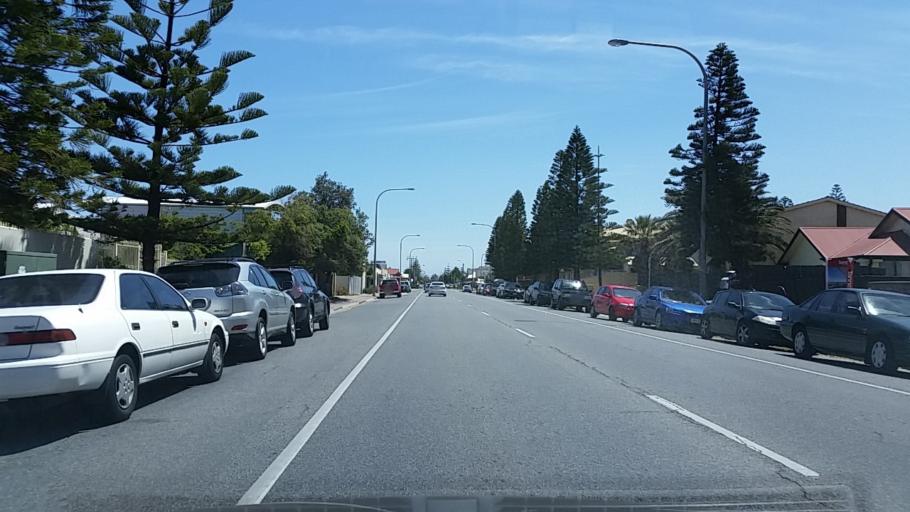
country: AU
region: South Australia
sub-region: Charles Sturt
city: Henley Beach
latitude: -34.9183
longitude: 138.4940
